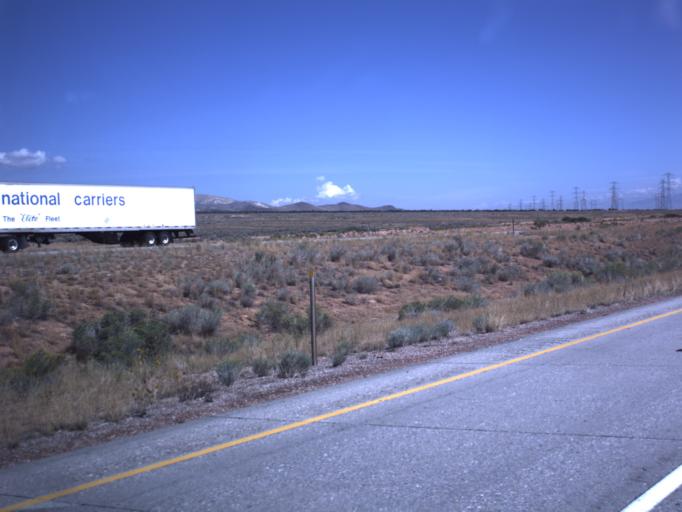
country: US
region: Utah
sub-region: Sevier County
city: Aurora
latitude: 38.8547
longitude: -111.9943
